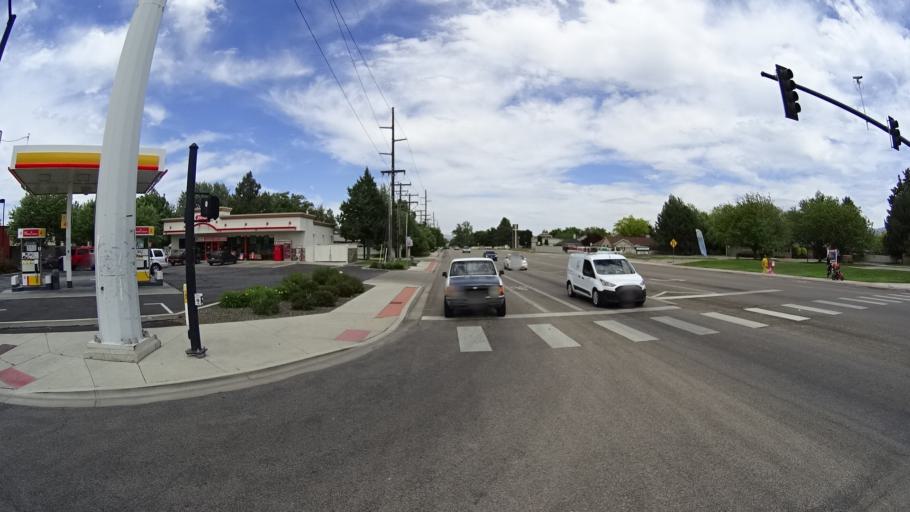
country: US
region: Idaho
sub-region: Ada County
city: Garden City
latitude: 43.6339
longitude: -116.2943
